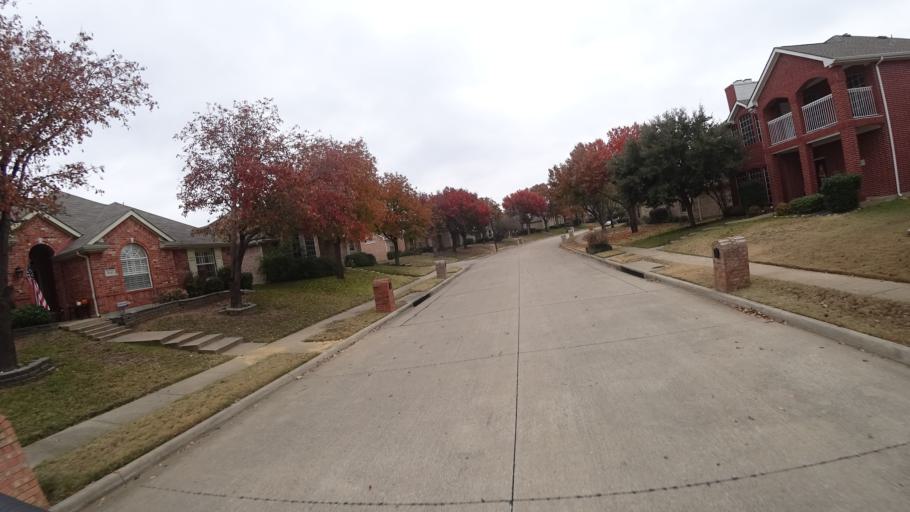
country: US
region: Texas
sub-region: Denton County
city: Lewisville
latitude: 33.0154
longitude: -96.9486
